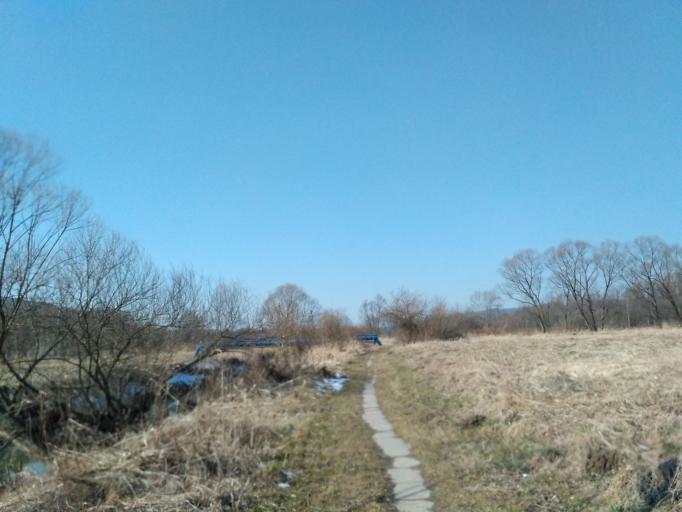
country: PL
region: Subcarpathian Voivodeship
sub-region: Powiat brzozowski
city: Domaradz
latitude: 49.7912
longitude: 21.9505
